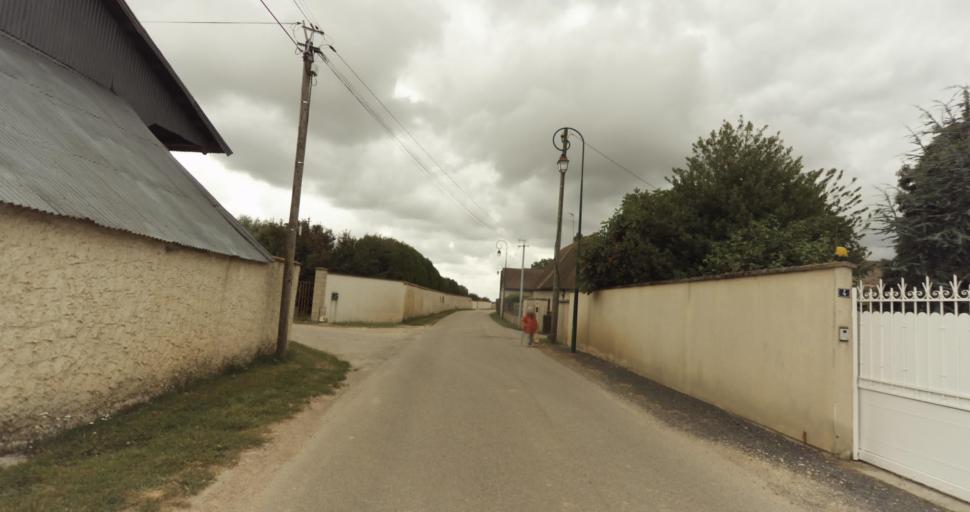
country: FR
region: Haute-Normandie
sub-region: Departement de l'Eure
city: Menilles
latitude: 49.0207
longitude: 1.2733
